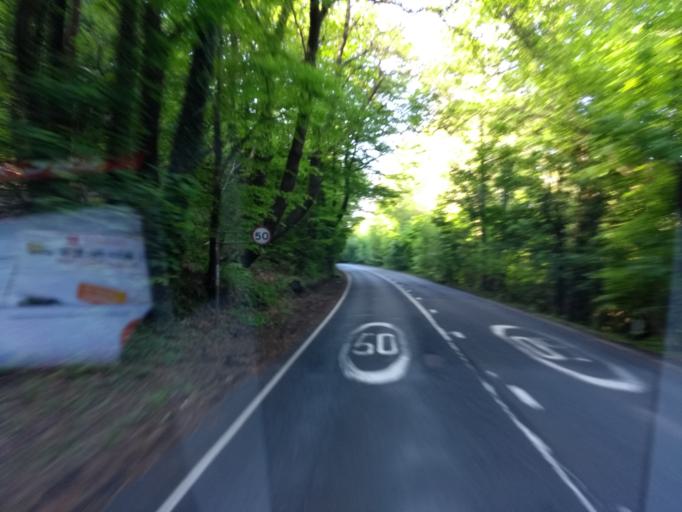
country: GB
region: England
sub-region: Devon
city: Honiton
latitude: 50.8446
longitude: -3.1342
